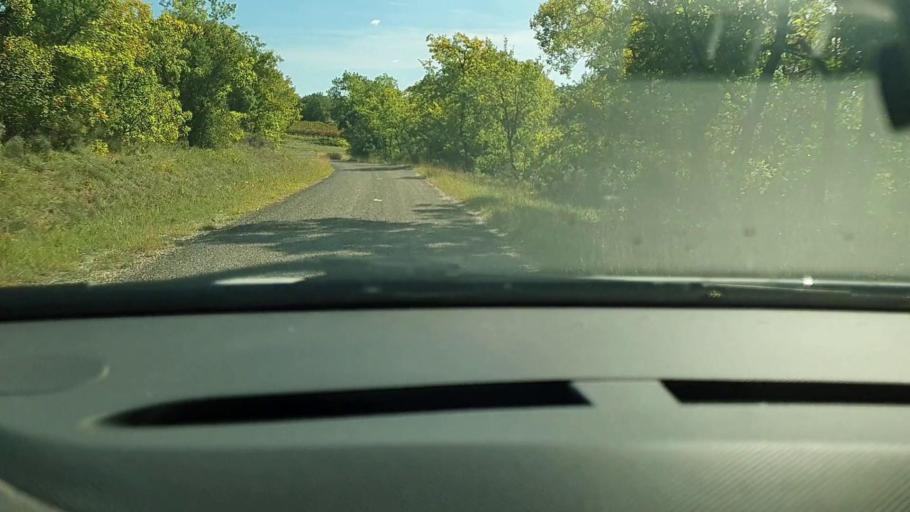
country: FR
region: Languedoc-Roussillon
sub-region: Departement du Gard
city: Barjac
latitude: 44.1954
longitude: 4.3147
